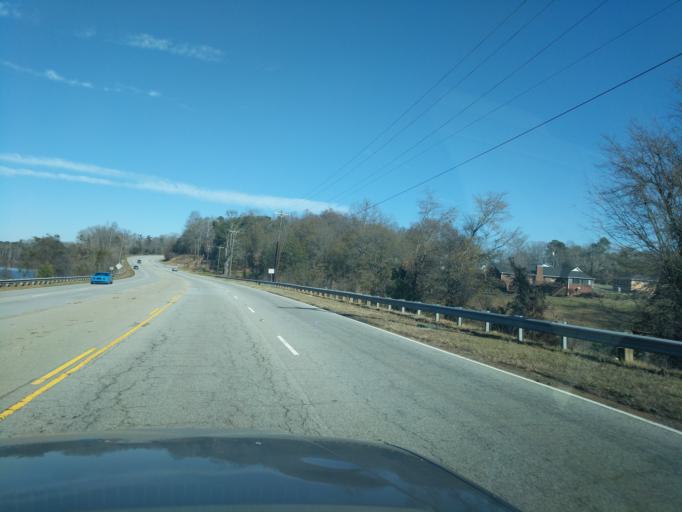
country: US
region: South Carolina
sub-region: Spartanburg County
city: Mayo
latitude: 35.0677
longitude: -81.8765
